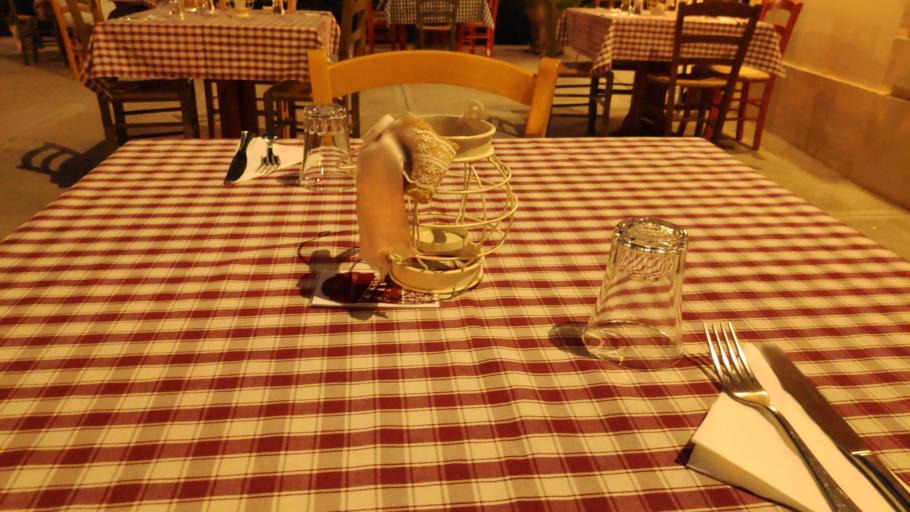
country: IT
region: Calabria
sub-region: Provincia di Reggio Calabria
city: Gioiosa Ionica
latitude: 38.3388
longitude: 16.3039
